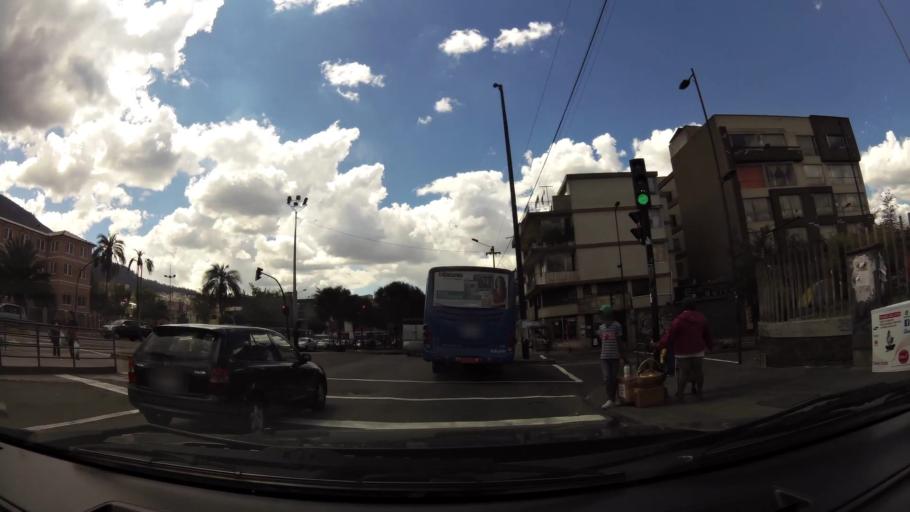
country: EC
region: Pichincha
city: Quito
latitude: -0.1964
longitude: -78.4996
